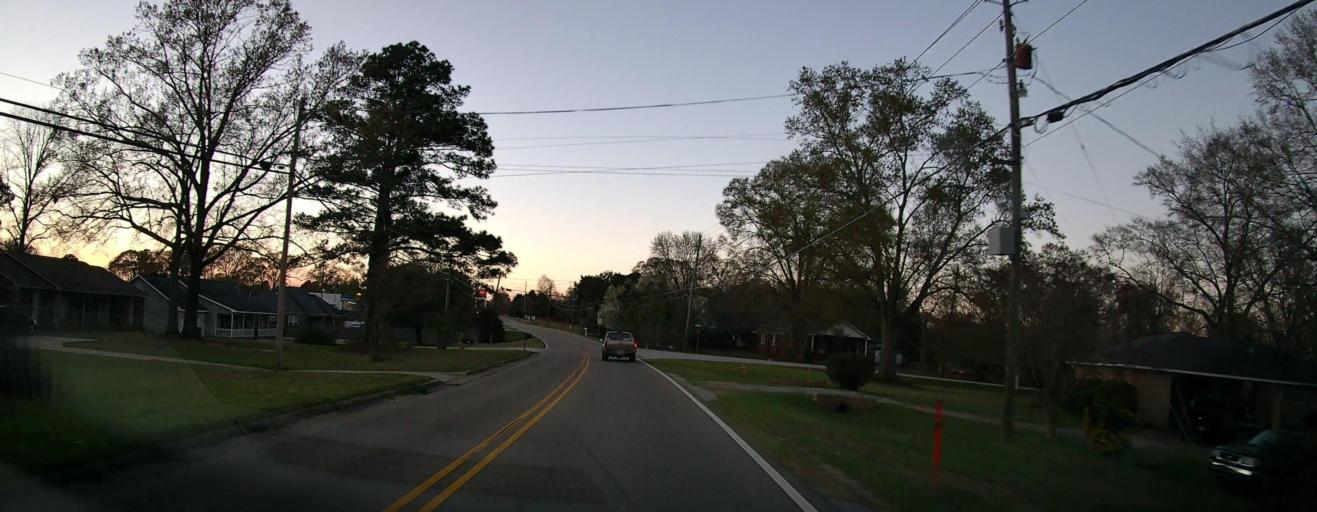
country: US
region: Alabama
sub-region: Russell County
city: Phenix City
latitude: 32.5108
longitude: -85.0204
